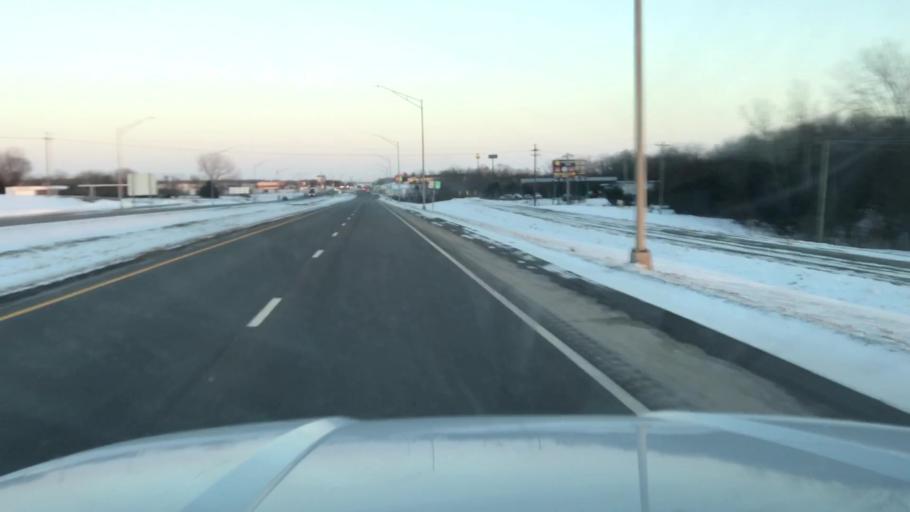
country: US
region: Missouri
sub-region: Clinton County
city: Cameron
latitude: 39.7540
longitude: -94.2270
